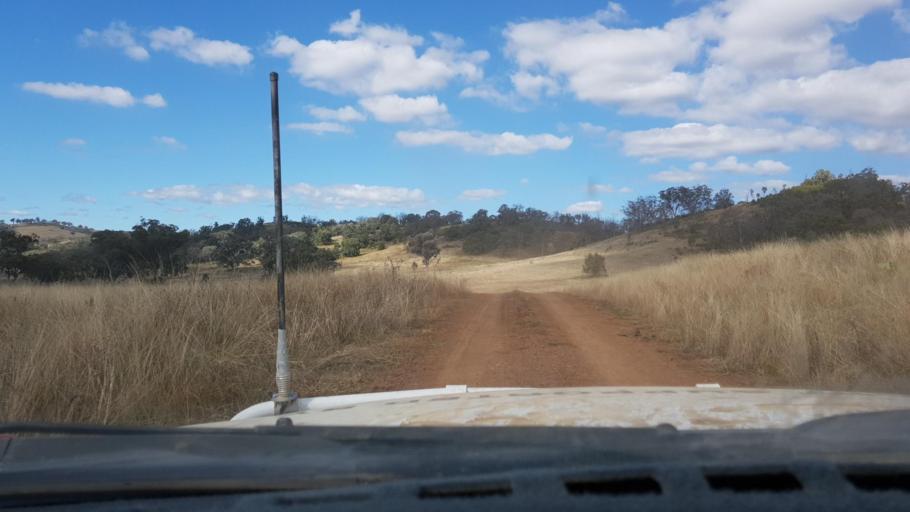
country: AU
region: New South Wales
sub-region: Tamworth Municipality
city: Manilla
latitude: -30.4384
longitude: 150.8282
